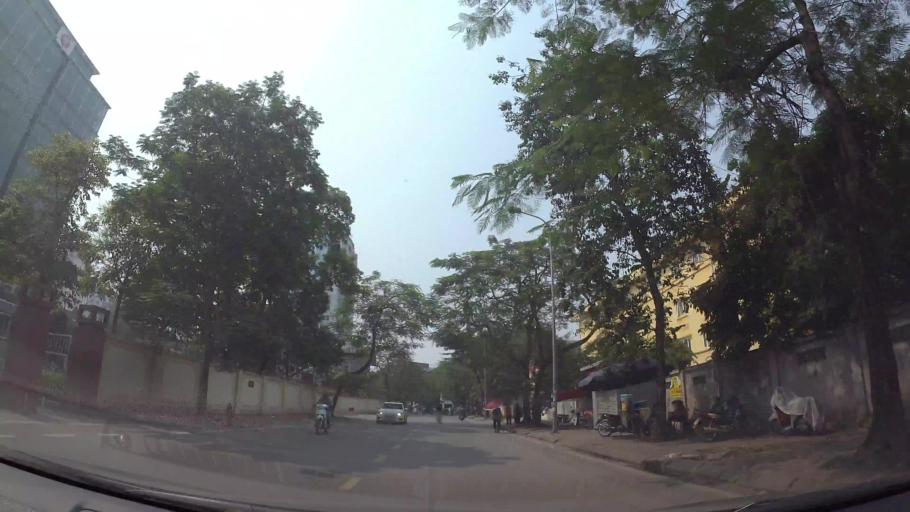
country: VN
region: Ha Noi
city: Dong Da
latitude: 21.0314
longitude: 105.8269
